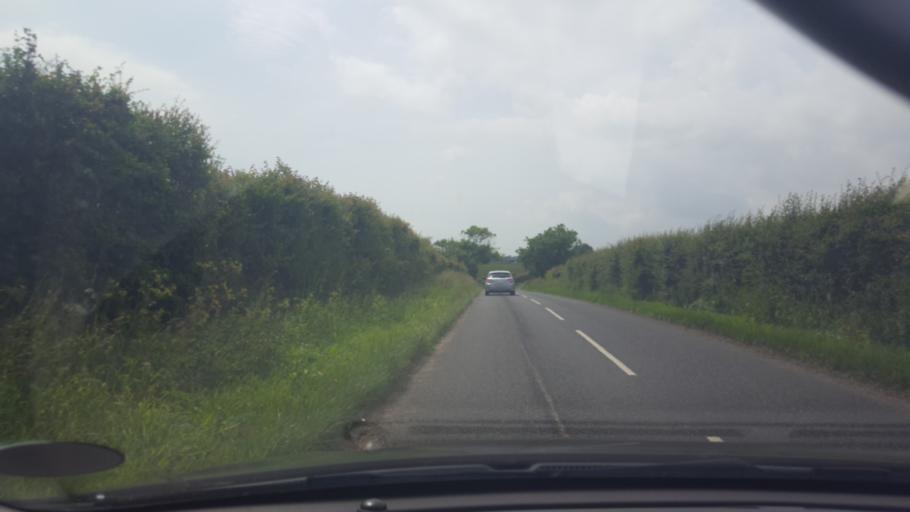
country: GB
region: England
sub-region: Essex
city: Clacton-on-Sea
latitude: 51.8142
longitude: 1.1856
